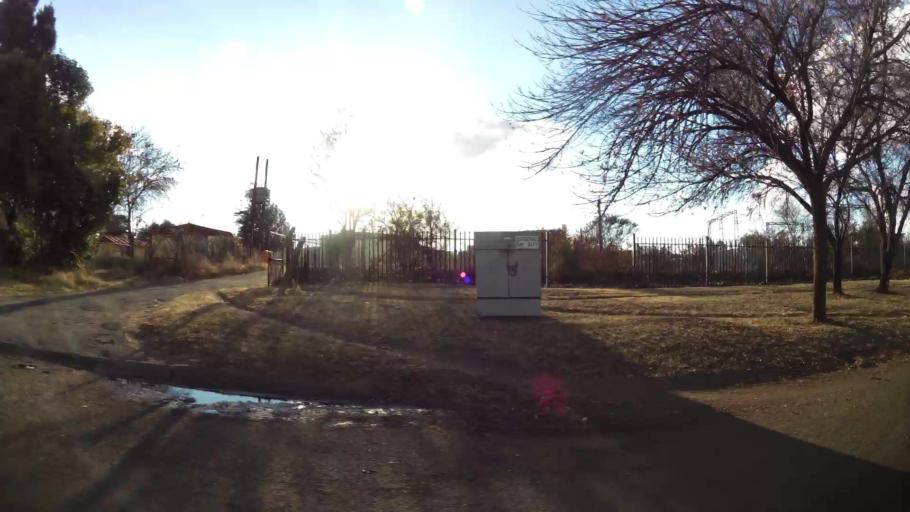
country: ZA
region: North-West
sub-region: Dr Kenneth Kaunda District Municipality
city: Potchefstroom
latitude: -26.7224
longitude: 27.0812
